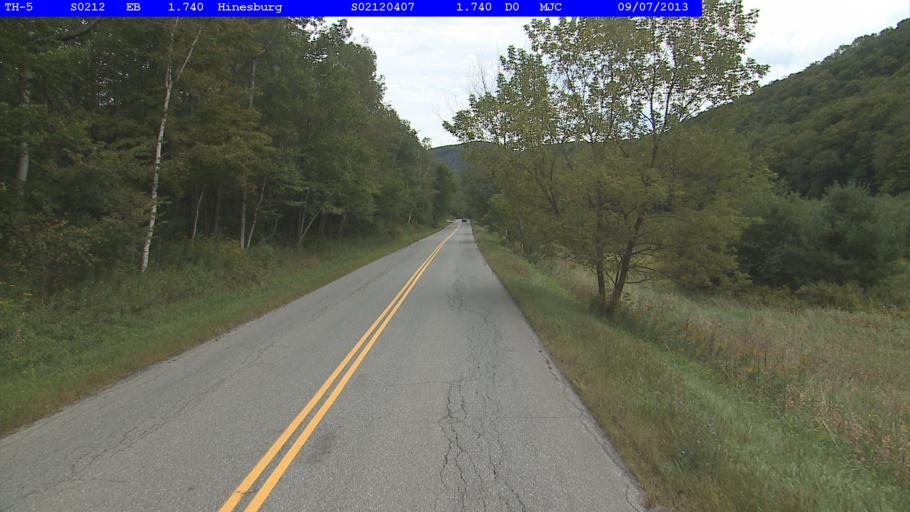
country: US
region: Vermont
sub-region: Chittenden County
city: Hinesburg
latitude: 44.2905
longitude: -73.0366
